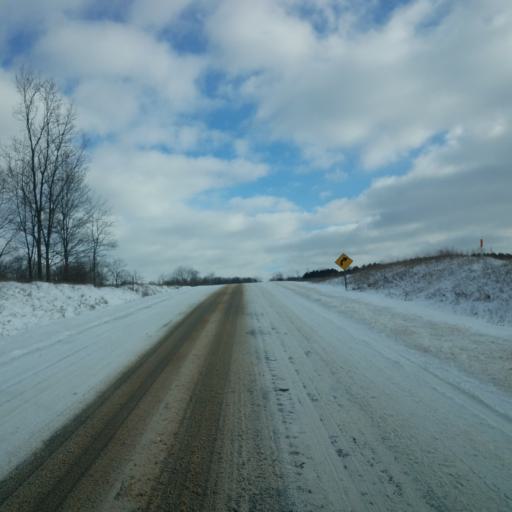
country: US
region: Michigan
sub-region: Osceola County
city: Reed City
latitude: 43.8501
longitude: -85.4191
